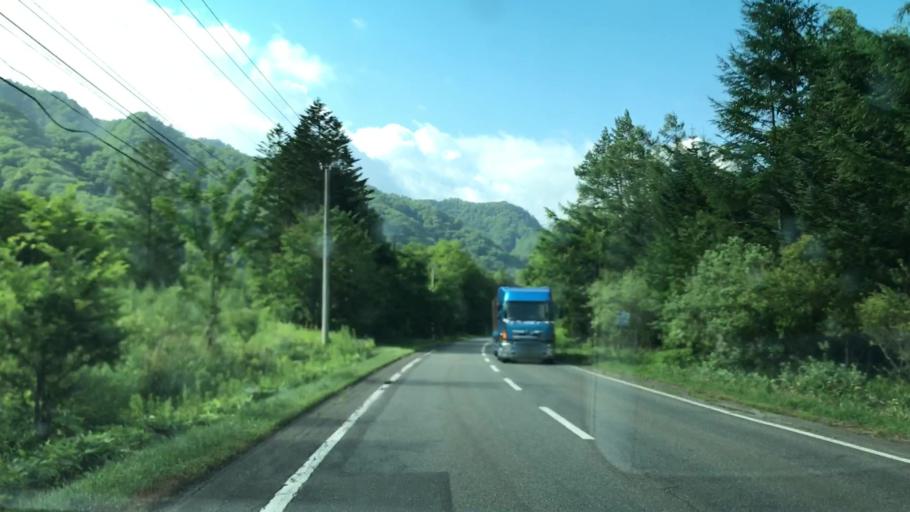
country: JP
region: Hokkaido
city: Shizunai-furukawacho
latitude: 42.8247
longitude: 142.4168
